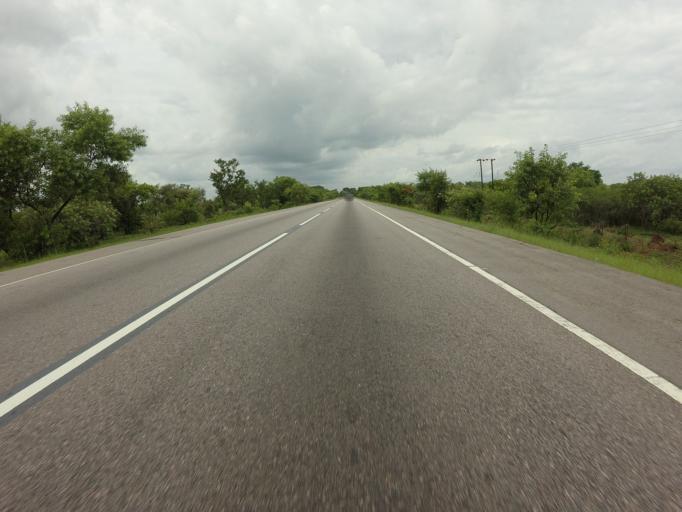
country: GH
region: Northern
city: Tamale
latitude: 8.8976
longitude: -1.4113
